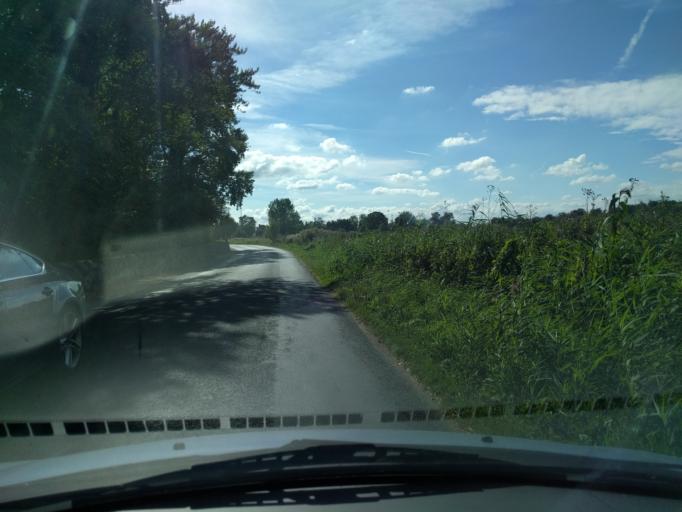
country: DK
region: South Denmark
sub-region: Kerteminde Kommune
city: Munkebo
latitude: 55.4267
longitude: 10.5831
